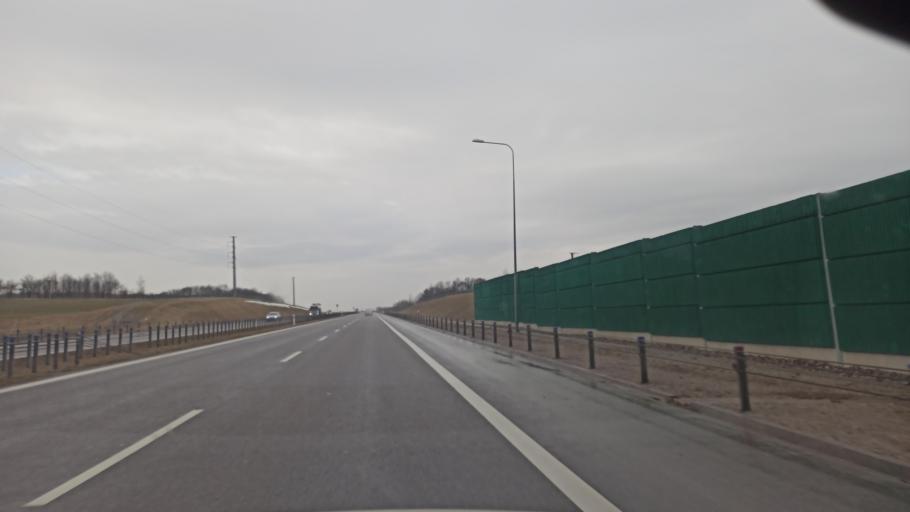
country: PL
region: Lublin Voivodeship
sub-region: Powiat lubelski
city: Kozubszczyzna
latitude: 51.2262
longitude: 22.4391
